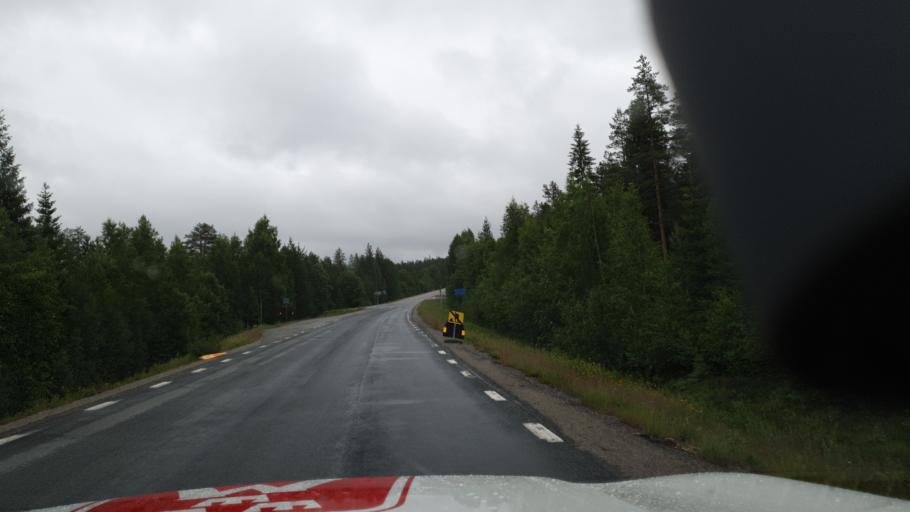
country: SE
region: Vaesterbotten
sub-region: Vannas Kommun
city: Vaennaes
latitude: 63.7849
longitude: 19.7438
